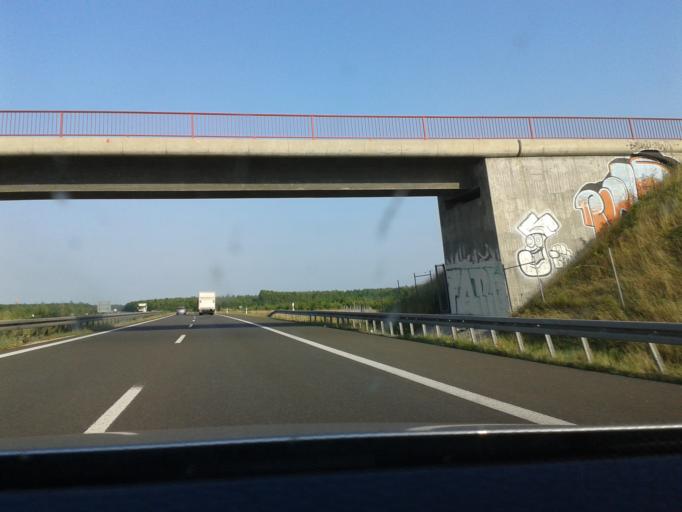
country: DE
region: Saxony
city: Zwenkau
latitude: 51.2481
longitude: 12.3197
